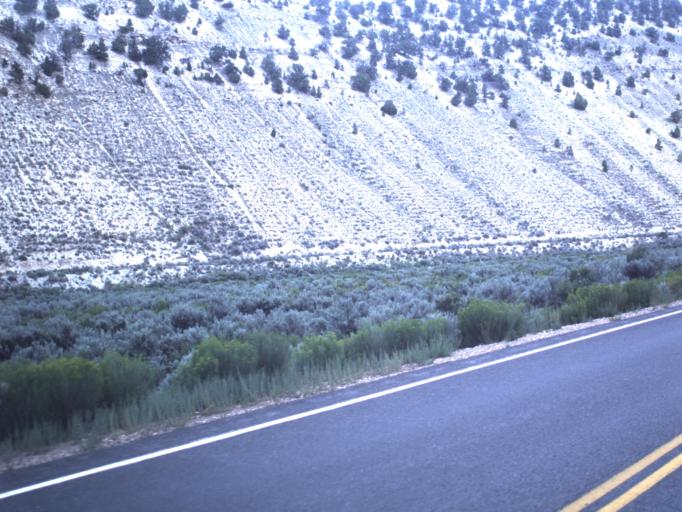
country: US
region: Utah
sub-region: Duchesne County
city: Duchesne
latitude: 40.0397
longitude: -110.5371
